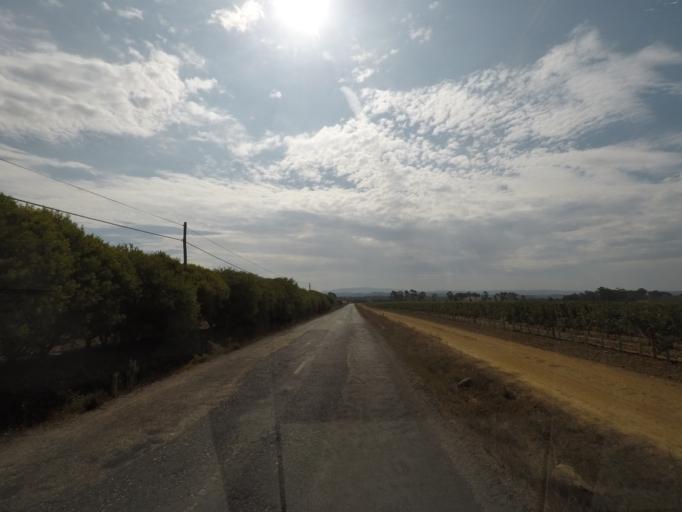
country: PT
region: Beja
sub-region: Odemira
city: Sao Teotonio
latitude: 37.4702
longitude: -8.7541
